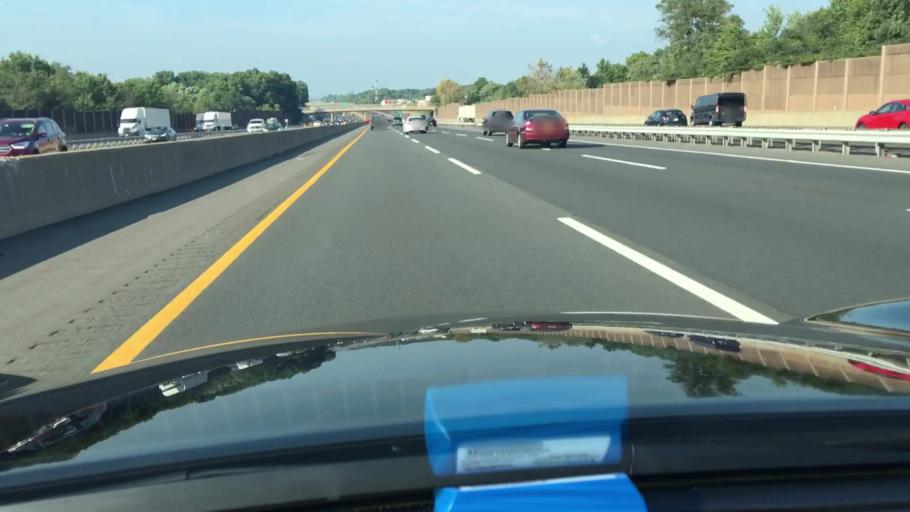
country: US
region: New Jersey
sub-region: Middlesex County
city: East Brunswick
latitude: 40.4355
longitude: -74.4314
